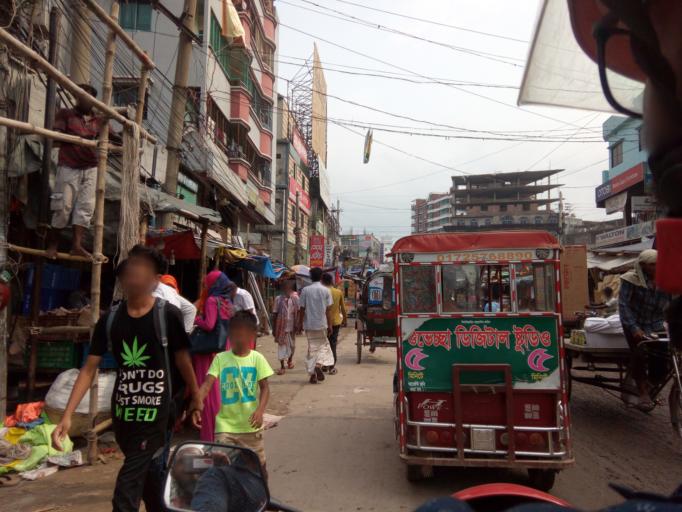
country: BD
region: Dhaka
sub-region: Dhaka
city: Dhaka
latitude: 23.7035
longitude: 90.4507
